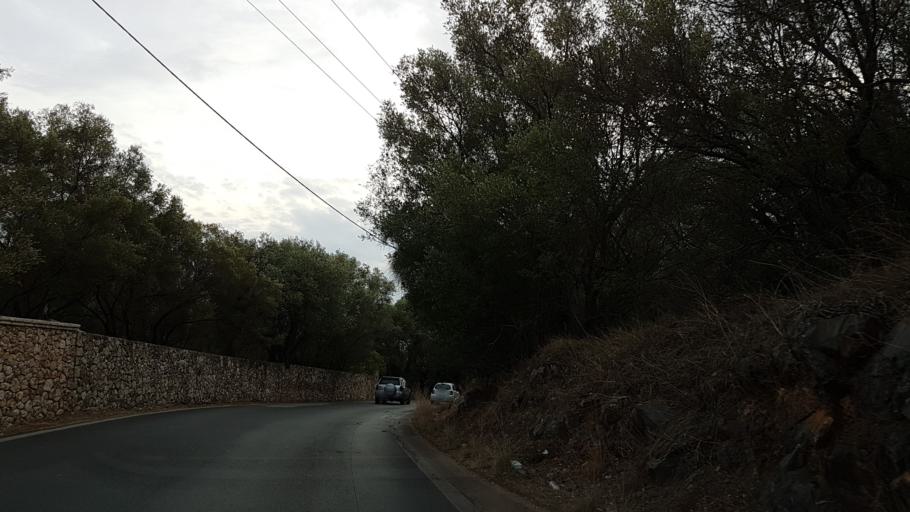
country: GR
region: Ionian Islands
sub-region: Nomos Kerkyras
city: Kontokali
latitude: 39.7114
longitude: 19.8588
